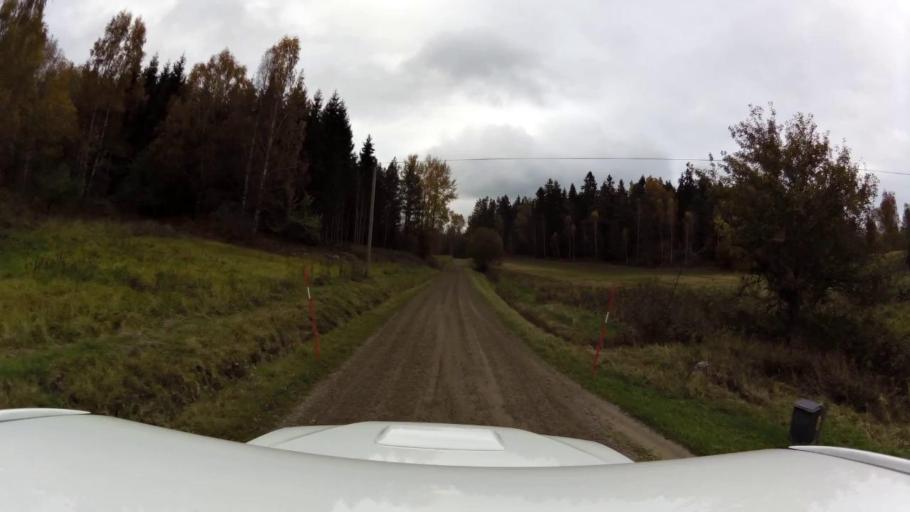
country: SE
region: OEstergoetland
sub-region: Linkopings Kommun
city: Ljungsbro
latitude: 58.5780
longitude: 15.4408
